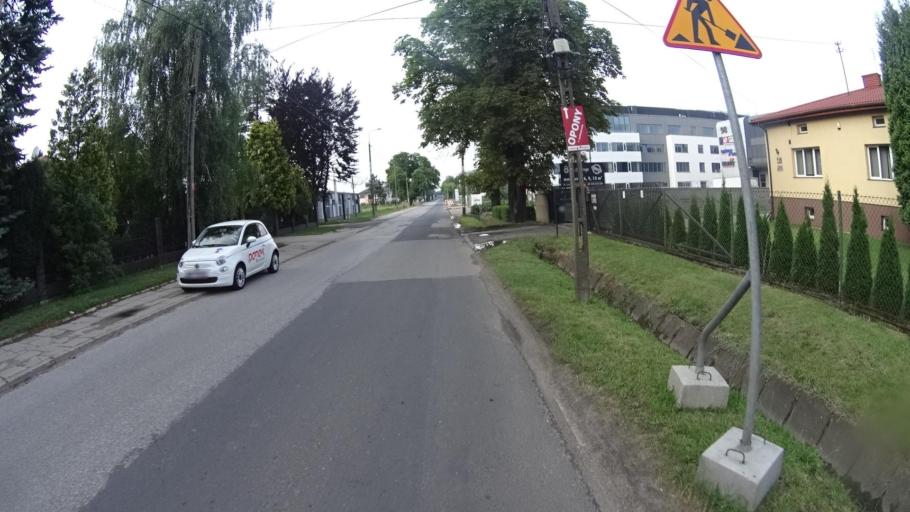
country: PL
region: Masovian Voivodeship
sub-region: Warszawa
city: Wlochy
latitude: 52.1899
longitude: 20.9271
